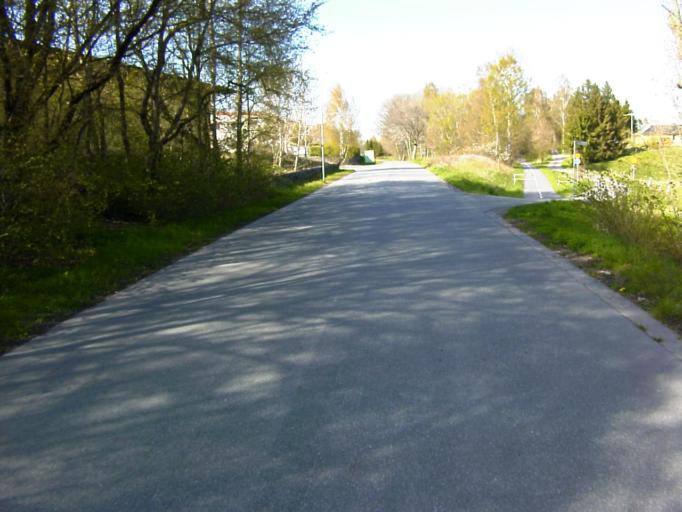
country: SE
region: Skane
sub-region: Kristianstads Kommun
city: Onnestad
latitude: 55.9954
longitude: 14.0375
